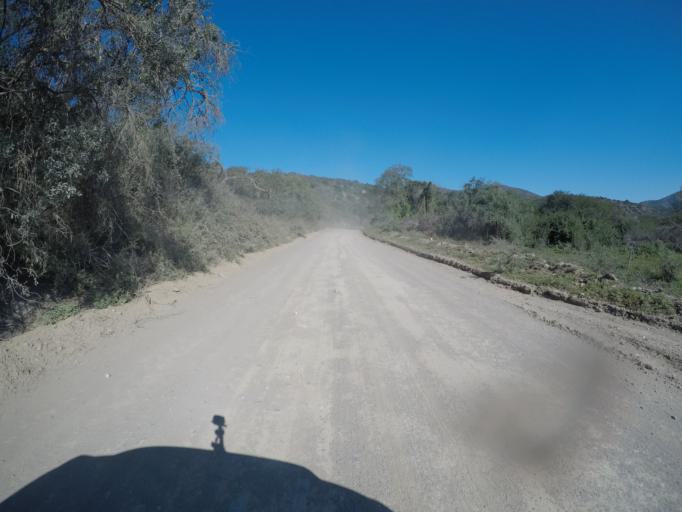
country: ZA
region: Eastern Cape
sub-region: Cacadu District Municipality
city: Kruisfontein
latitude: -33.6707
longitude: 24.5747
